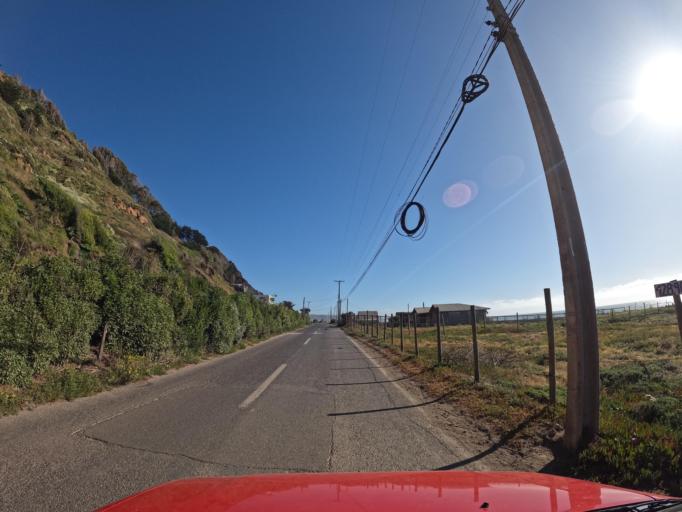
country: CL
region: Maule
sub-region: Provincia de Talca
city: Constitucion
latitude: -34.8576
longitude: -72.1456
